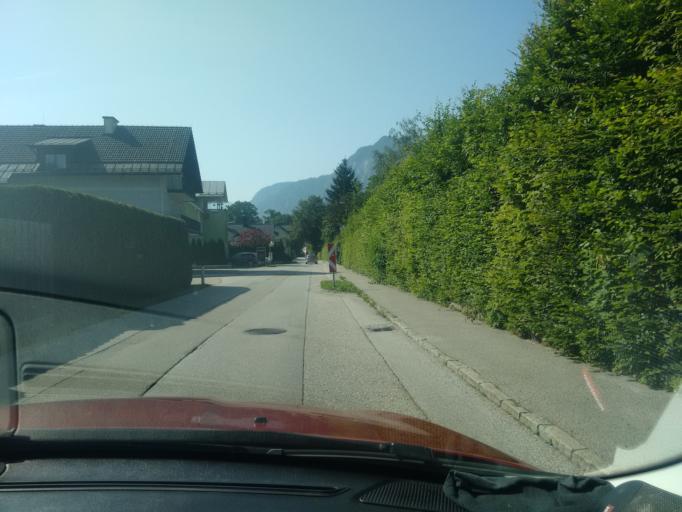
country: AT
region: Upper Austria
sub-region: Politischer Bezirk Gmunden
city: Bad Goisern
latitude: 47.6478
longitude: 13.6134
